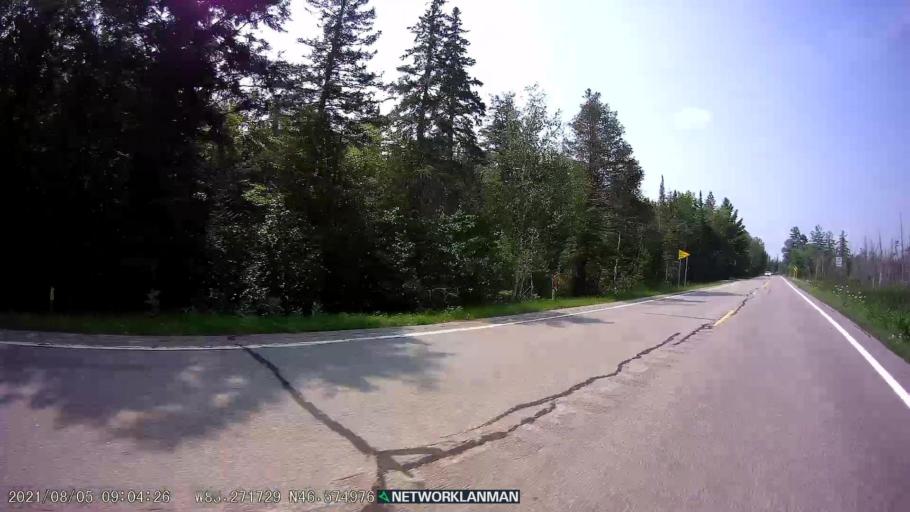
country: US
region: Michigan
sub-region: Luce County
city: Newberry
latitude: 46.5747
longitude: -85.2719
